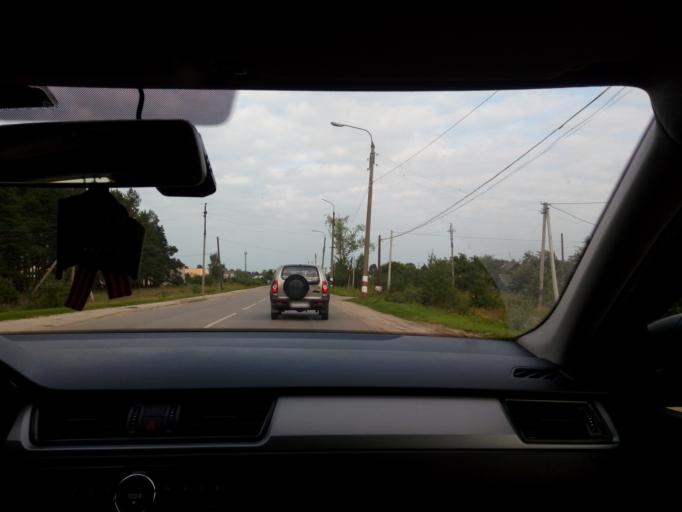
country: RU
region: Nizjnij Novgorod
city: Voskresenskoye
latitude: 56.8390
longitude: 45.4208
